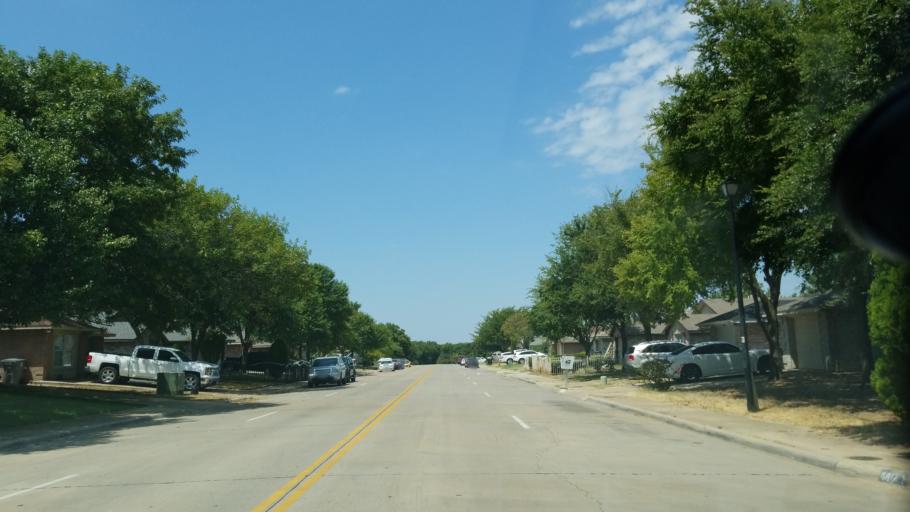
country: US
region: Texas
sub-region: Dallas County
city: Cockrell Hill
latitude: 32.7297
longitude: -96.8944
